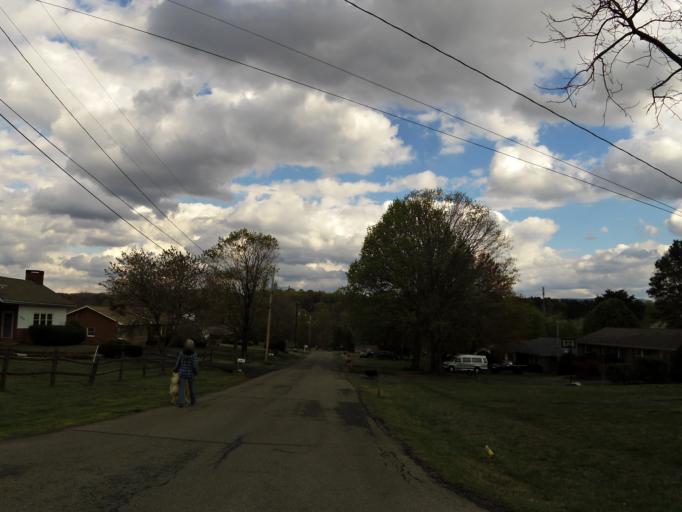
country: US
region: Tennessee
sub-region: Blount County
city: Maryville
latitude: 35.7398
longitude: -83.9795
